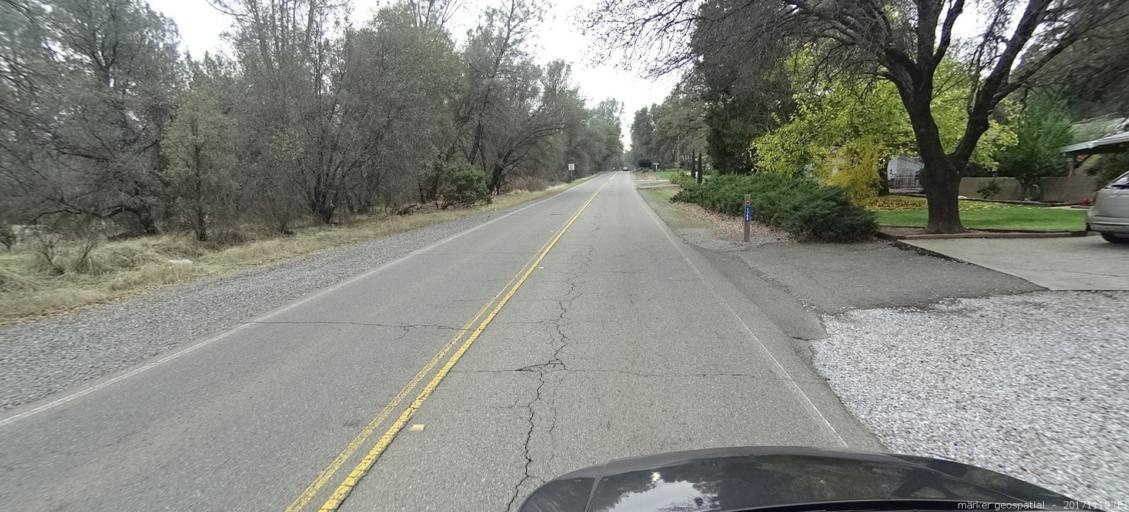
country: US
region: California
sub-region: Shasta County
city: Redding
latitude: 40.4993
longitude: -122.3837
